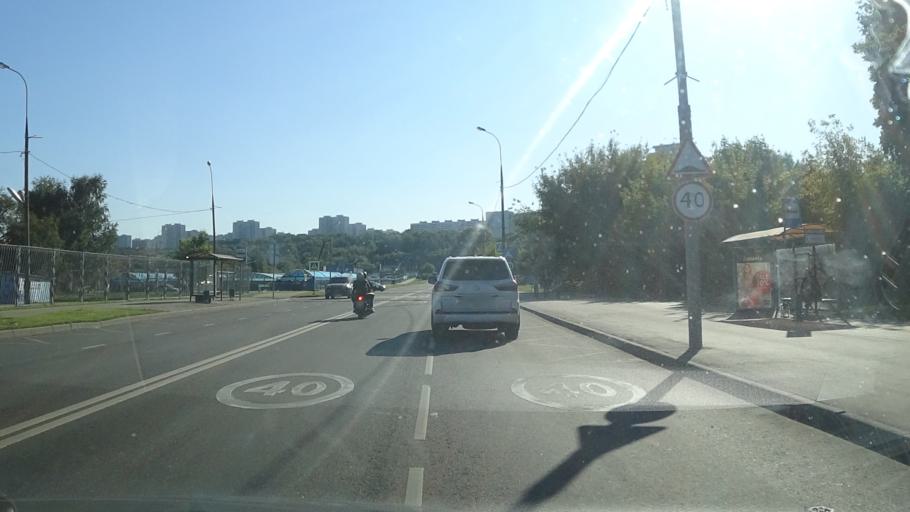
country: RU
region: Moskovskaya
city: Bol'shaya Setun'
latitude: 55.7547
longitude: 37.4329
